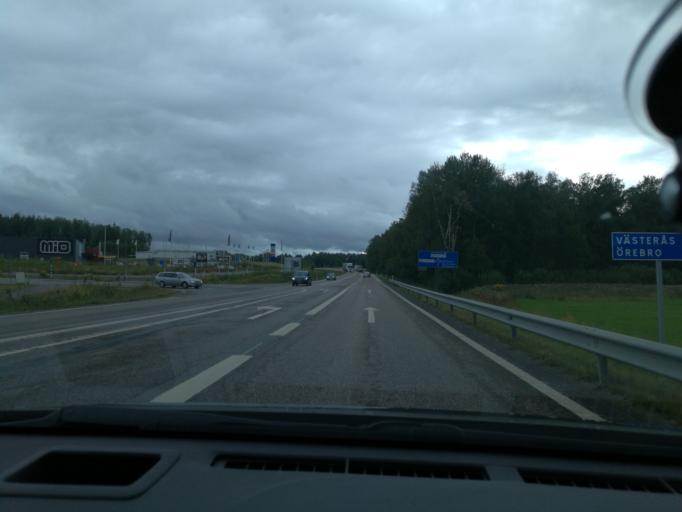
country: SE
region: Soedermanland
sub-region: Katrineholms Kommun
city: Katrineholm
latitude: 59.0074
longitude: 16.2347
